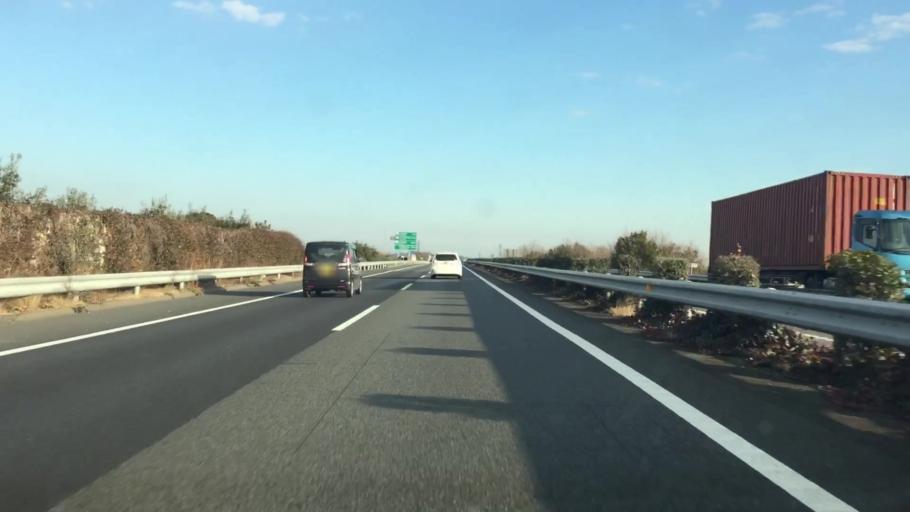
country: JP
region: Gunma
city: Isesaki
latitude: 36.3524
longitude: 139.2297
